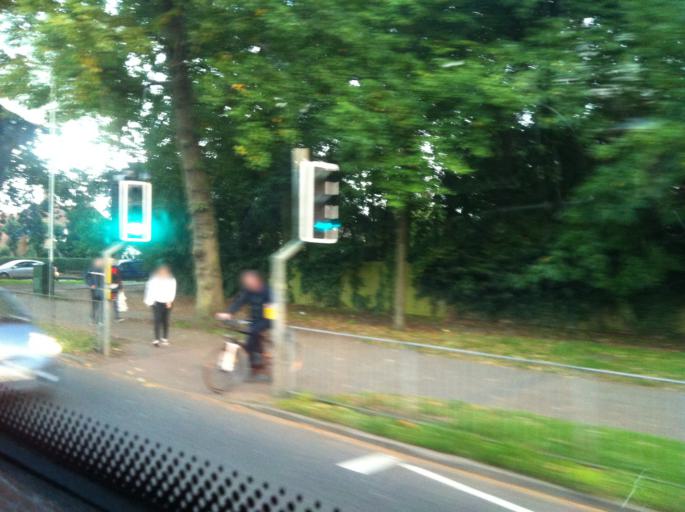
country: GB
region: England
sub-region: Norfolk
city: Cringleford
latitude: 52.6288
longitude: 1.2475
